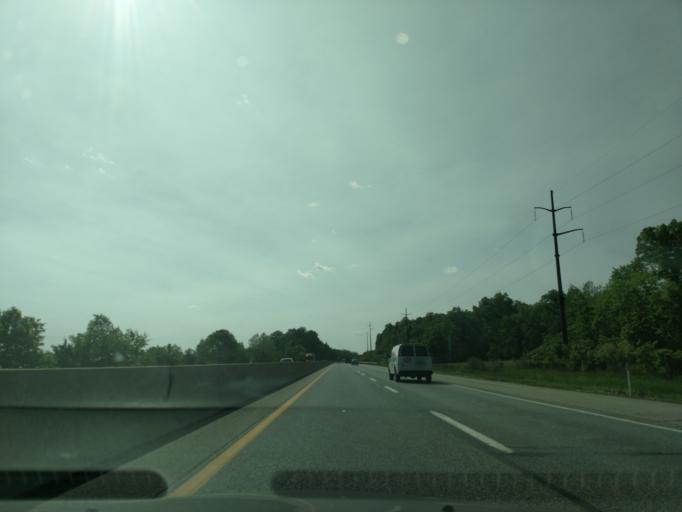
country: US
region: Pennsylvania
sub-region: Lancaster County
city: Reamstown
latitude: 40.2259
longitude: -76.1056
